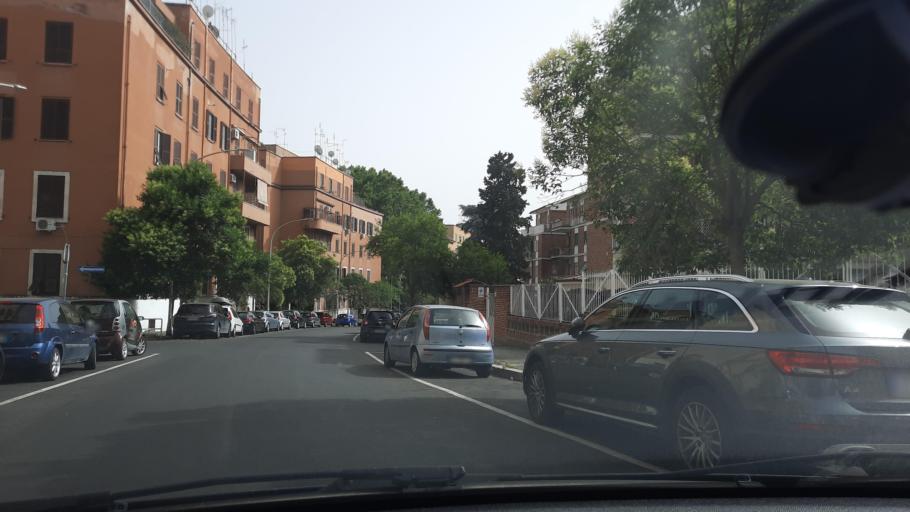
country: IT
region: Latium
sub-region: Citta metropolitana di Roma Capitale
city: Rome
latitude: 41.8595
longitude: 12.4900
